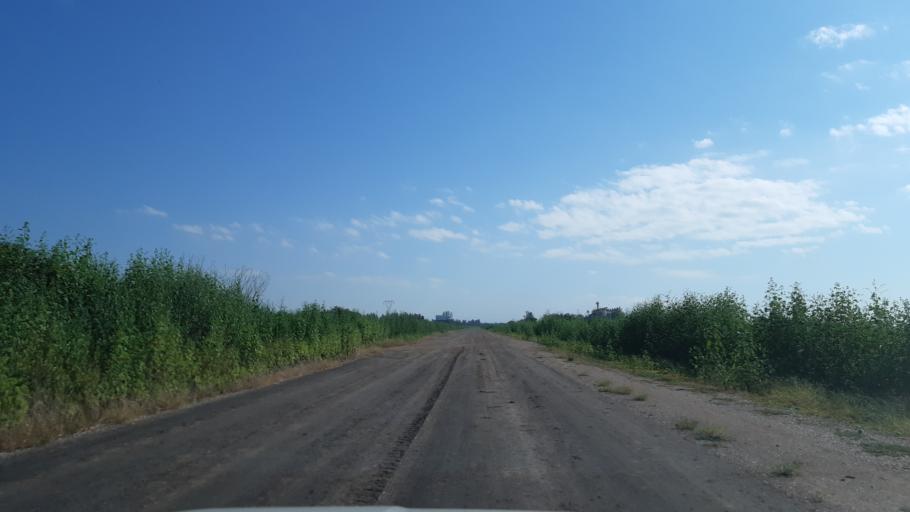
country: AR
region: Salta
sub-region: Departamento de General Guemes
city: General Martin Miguel de Guemes
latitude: -24.5475
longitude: -65.0792
